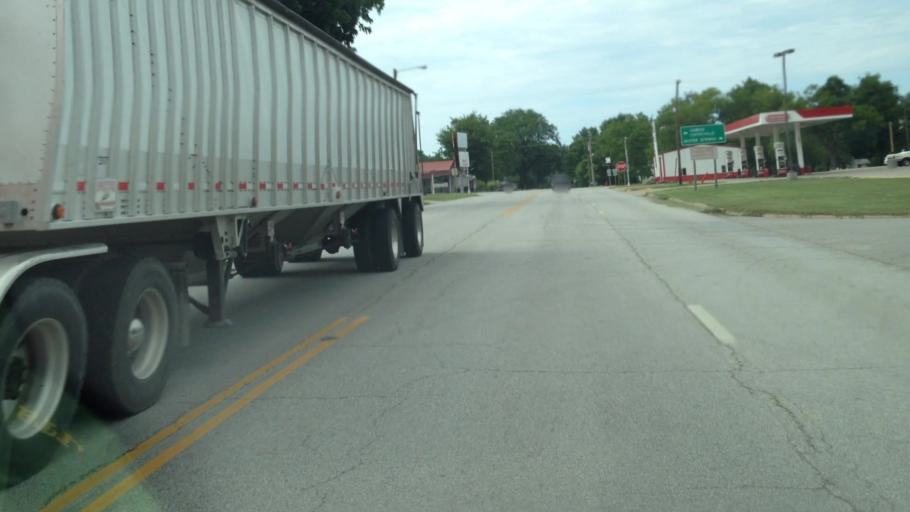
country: US
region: Kansas
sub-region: Labette County
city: Chetopa
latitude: 37.0357
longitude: -95.0861
